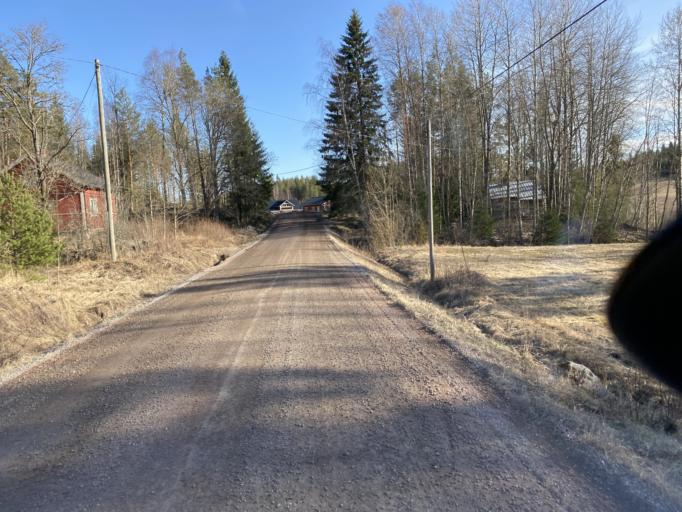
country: FI
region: Satakunta
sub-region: Rauma
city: Lappi
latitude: 61.1434
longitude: 21.9297
